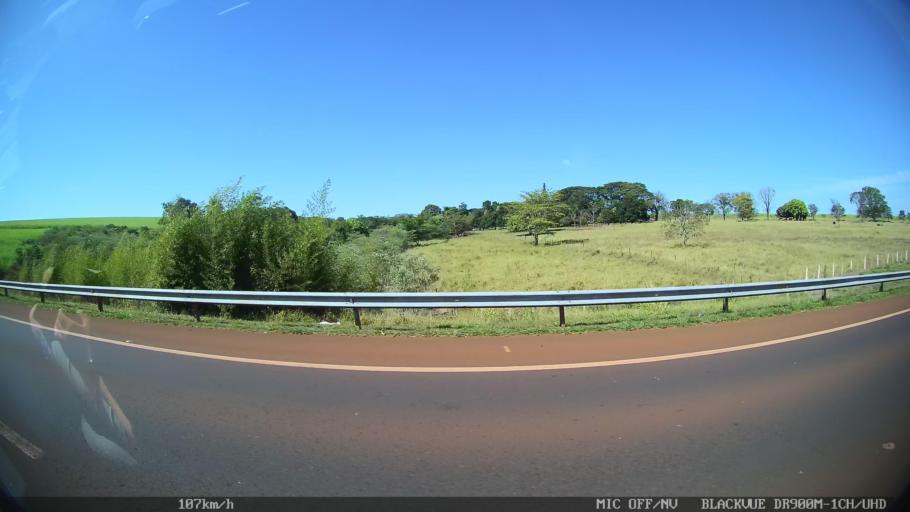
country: BR
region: Sao Paulo
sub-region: Franca
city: Franca
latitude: -20.6560
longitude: -47.4909
